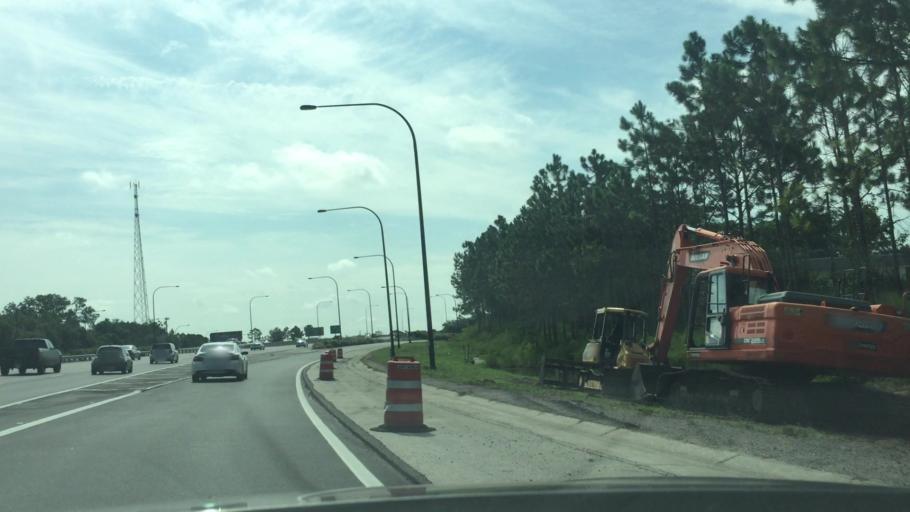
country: US
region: Florida
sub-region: Orange County
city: Orlovista
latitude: 28.5489
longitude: -81.4655
